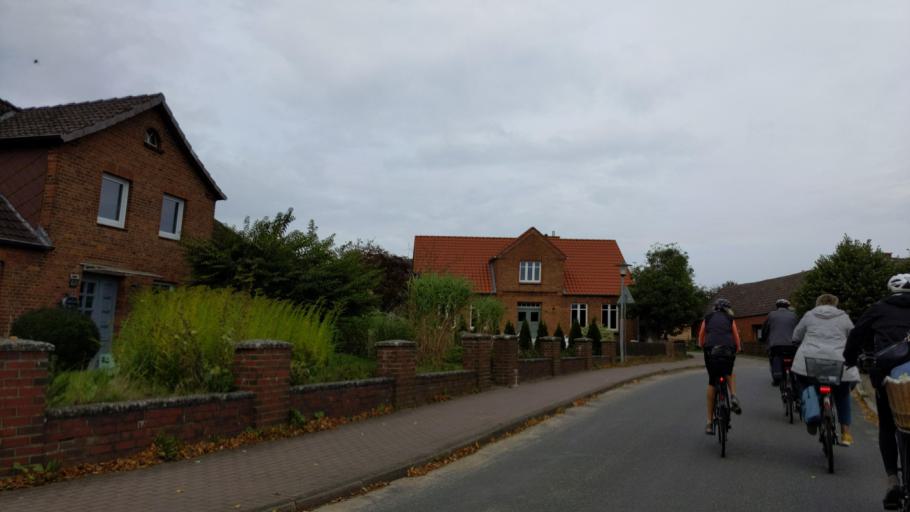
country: DE
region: Schleswig-Holstein
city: Bak
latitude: 53.7158
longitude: 10.7867
